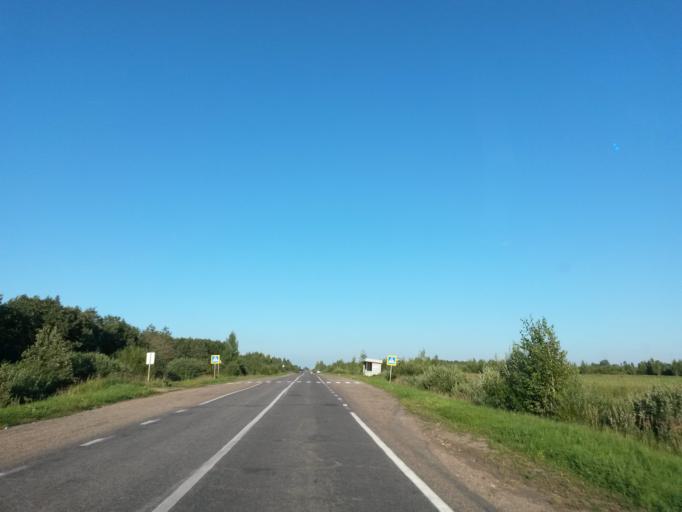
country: RU
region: Jaroslavl
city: Gavrilov-Yam
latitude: 57.3076
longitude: 39.8930
